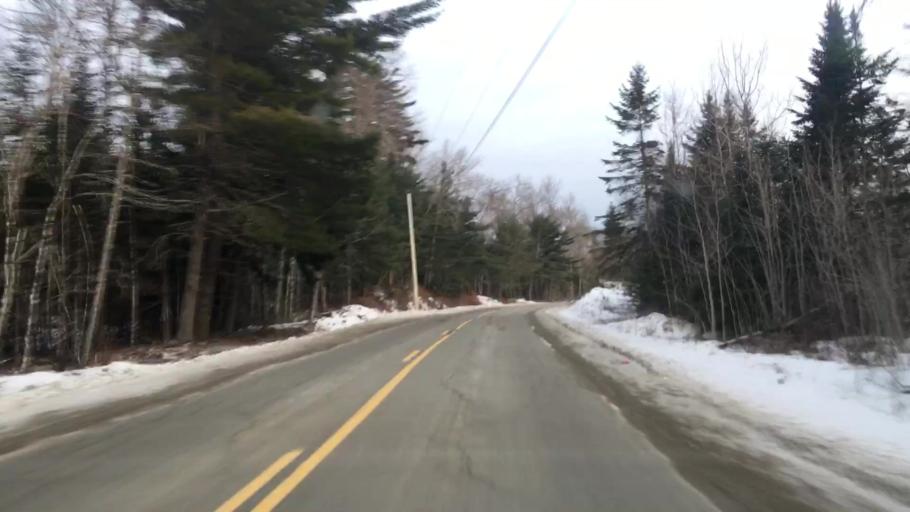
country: US
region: Maine
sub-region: Hancock County
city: Franklin
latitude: 44.7576
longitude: -68.3245
